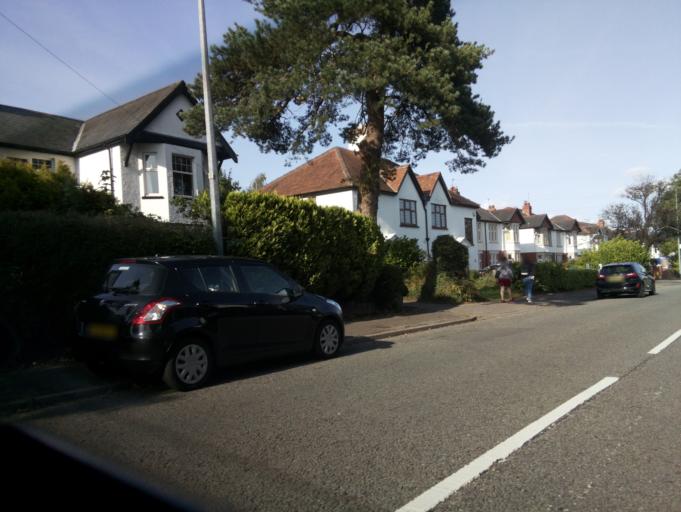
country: GB
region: Wales
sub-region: Cardiff
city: Cardiff
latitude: 51.5247
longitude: -3.2048
